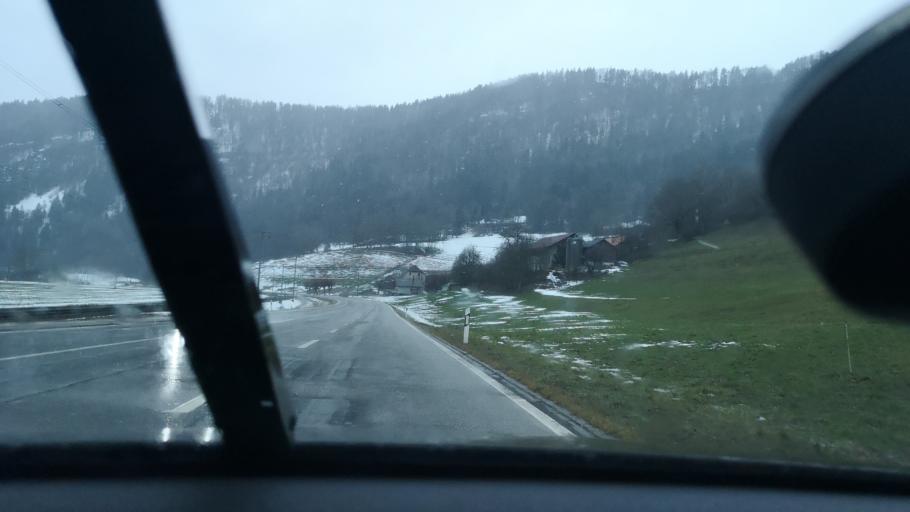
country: CH
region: Neuchatel
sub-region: Val-de-Travers District
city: Travers
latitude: 46.9570
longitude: 6.7071
